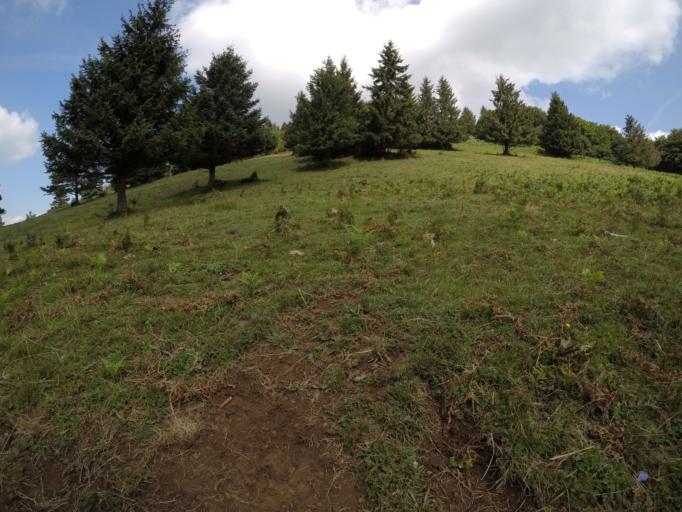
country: FR
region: Auvergne
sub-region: Departement du Puy-de-Dome
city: Aydat
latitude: 45.7065
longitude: 2.9334
